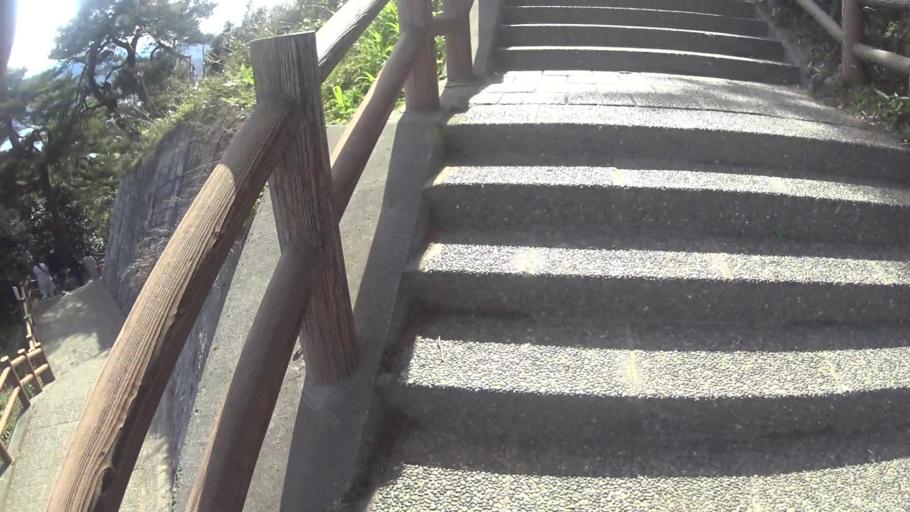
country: JP
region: Kyoto
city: Miyazu
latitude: 35.5869
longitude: 135.1949
